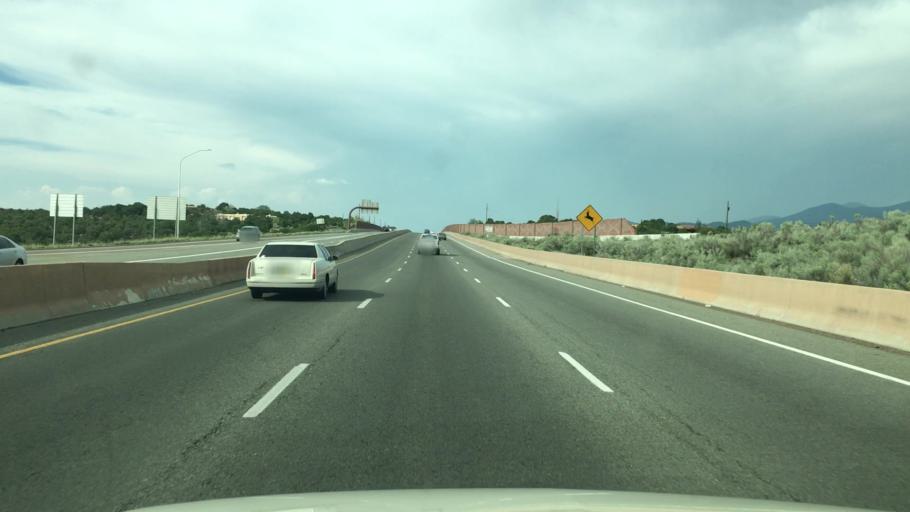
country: US
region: New Mexico
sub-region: Santa Fe County
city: Santa Fe
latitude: 35.7140
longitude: -105.9374
